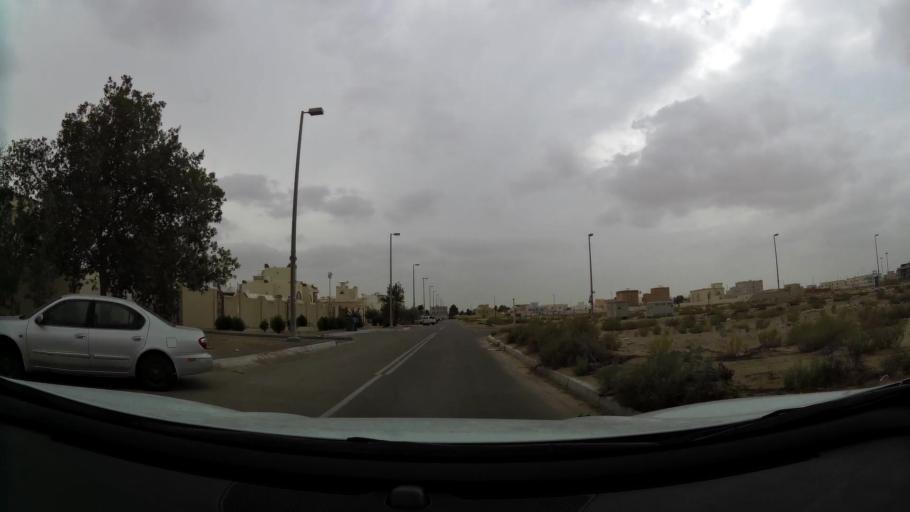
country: AE
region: Abu Dhabi
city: Abu Dhabi
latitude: 24.3880
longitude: 54.6528
